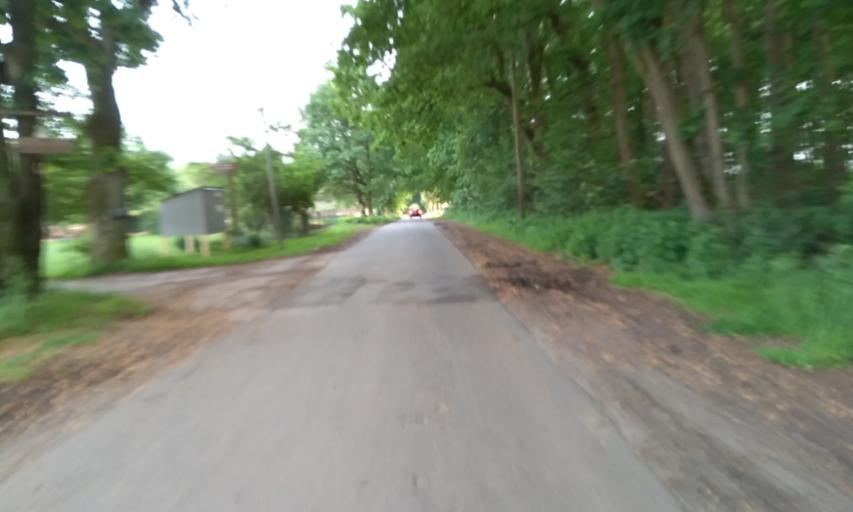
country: DE
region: Lower Saxony
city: Bargstedt
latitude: 53.4861
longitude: 9.4642
